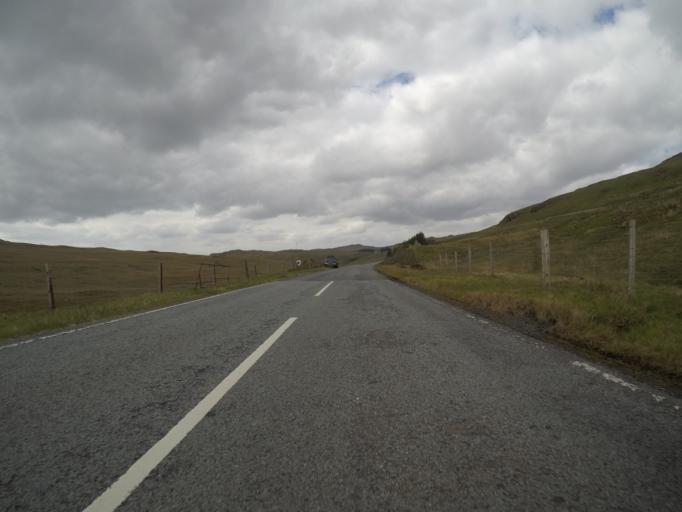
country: GB
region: Scotland
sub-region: Highland
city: Isle of Skye
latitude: 57.3218
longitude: -6.3280
